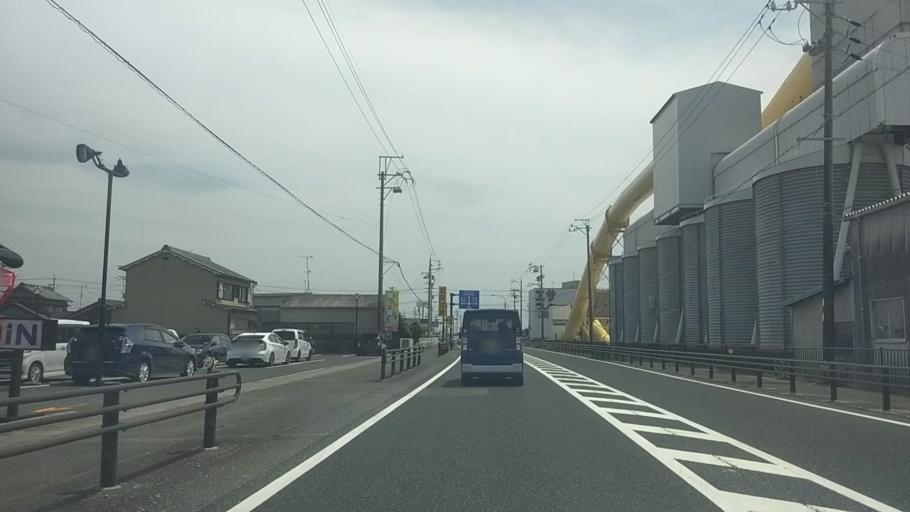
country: JP
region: Shizuoka
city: Kosai-shi
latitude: 34.6814
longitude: 137.6264
